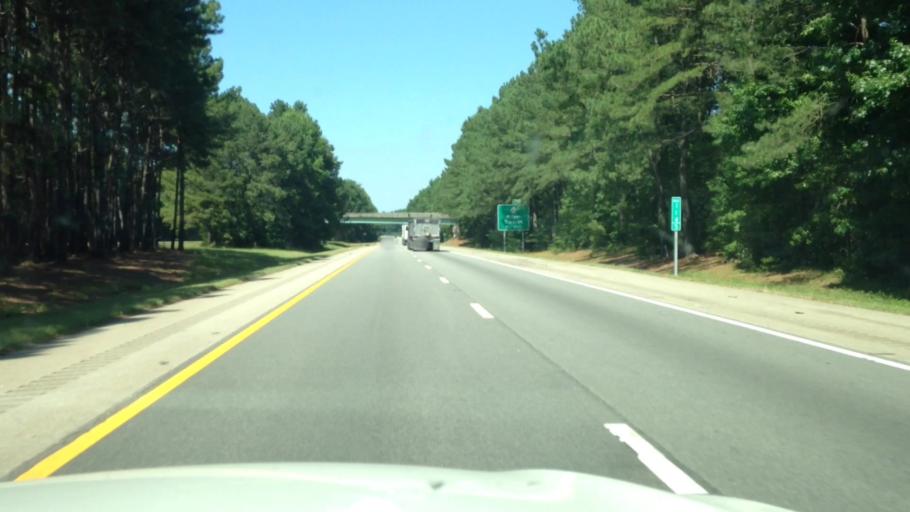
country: US
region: North Carolina
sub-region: Wilson County
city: Lucama
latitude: 35.6804
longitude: -78.0644
